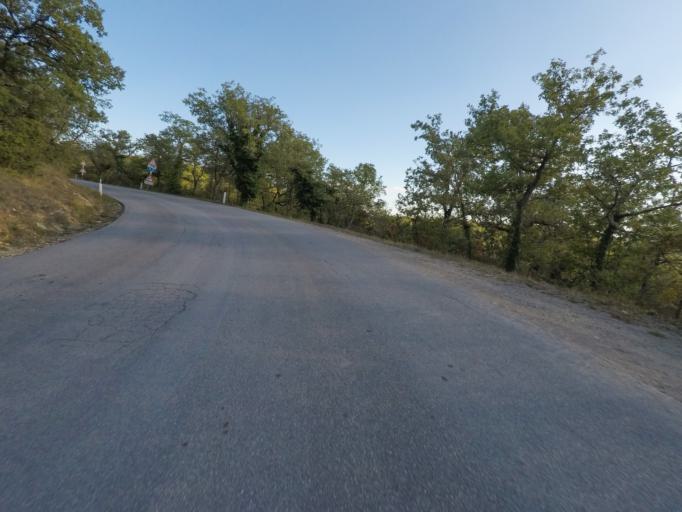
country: IT
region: Tuscany
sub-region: Provincia di Siena
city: Radda in Chianti
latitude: 43.4544
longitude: 11.3835
